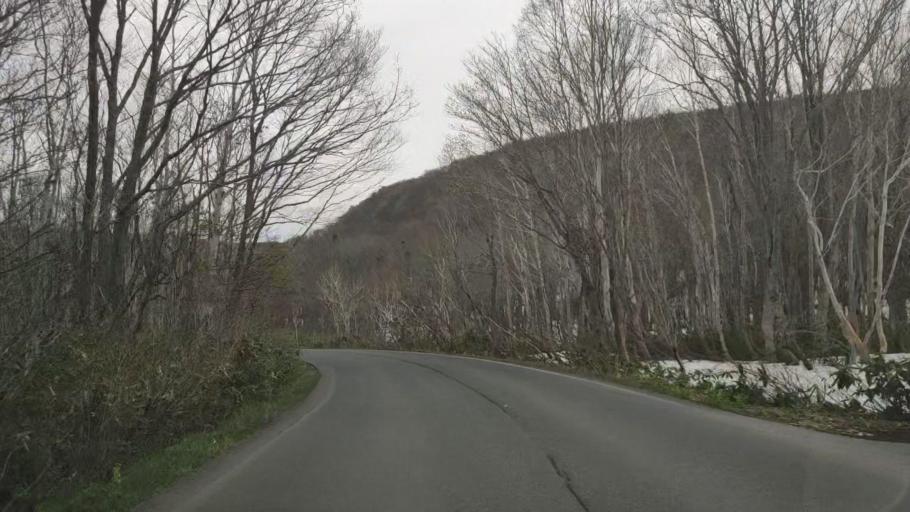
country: JP
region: Aomori
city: Aomori Shi
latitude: 40.6932
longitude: 140.9089
